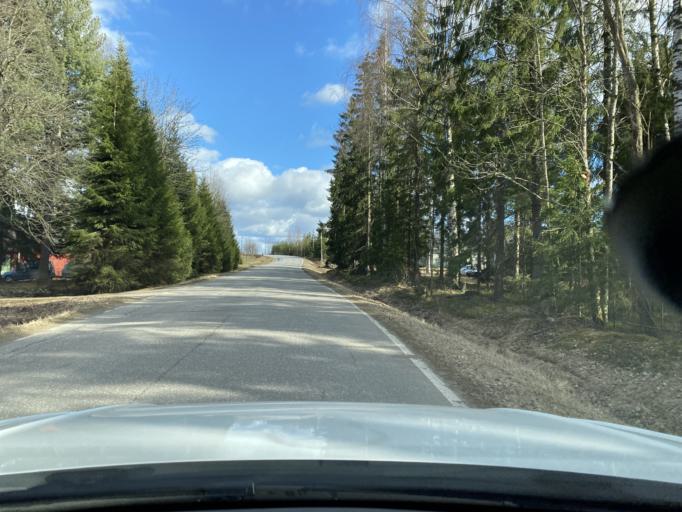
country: FI
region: Pirkanmaa
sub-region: Lounais-Pirkanmaa
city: Punkalaidun
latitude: 61.0956
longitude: 23.1320
